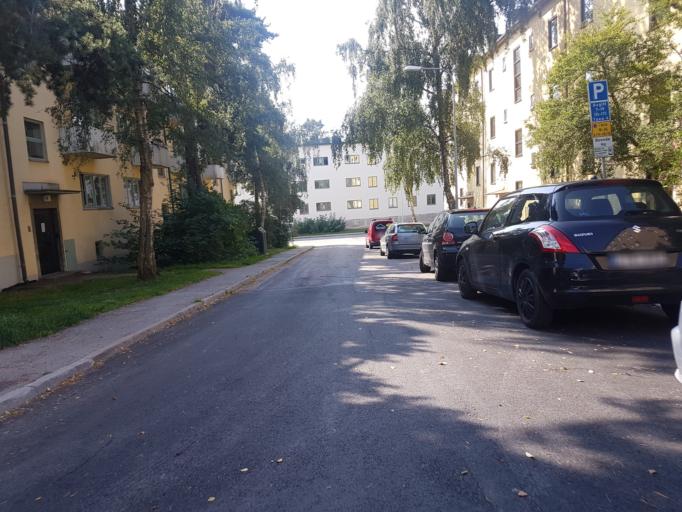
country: SE
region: Stockholm
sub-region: Stockholms Kommun
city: OEstermalm
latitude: 59.2982
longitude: 18.0979
